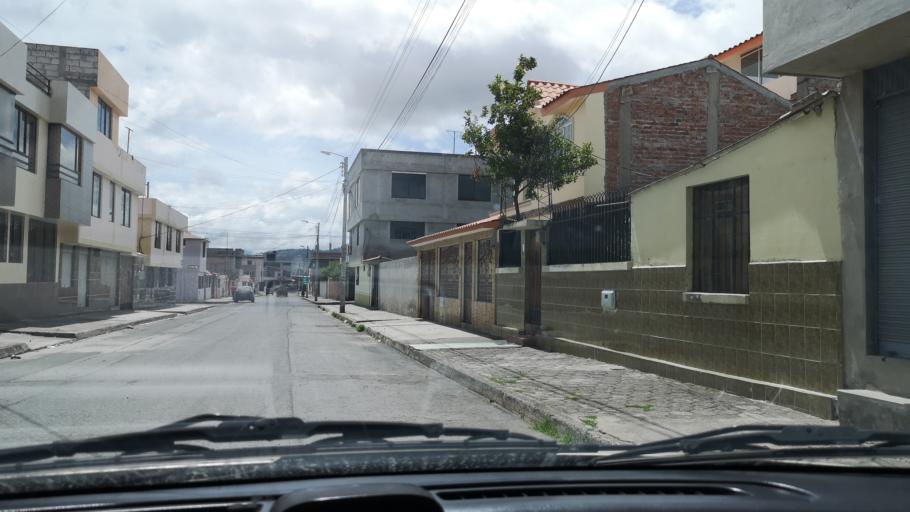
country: EC
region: Chimborazo
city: Riobamba
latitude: -1.6451
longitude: -78.6835
